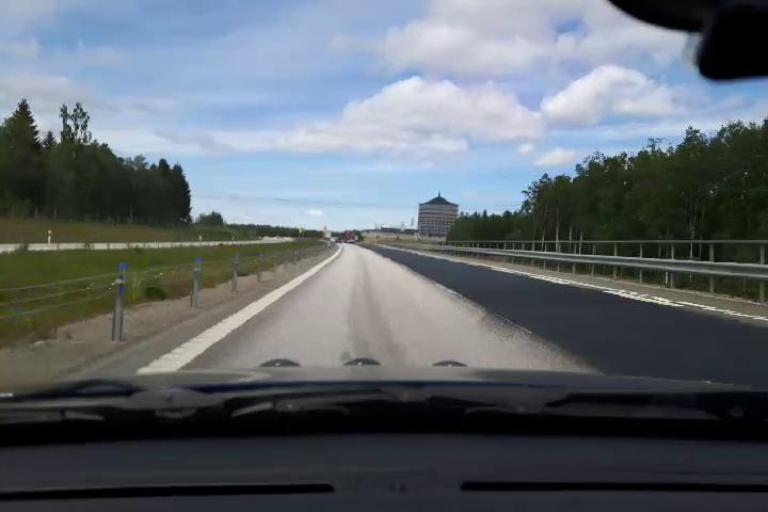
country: SE
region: Uppsala
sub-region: Alvkarleby Kommun
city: AElvkarleby
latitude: 60.4583
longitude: 17.4150
